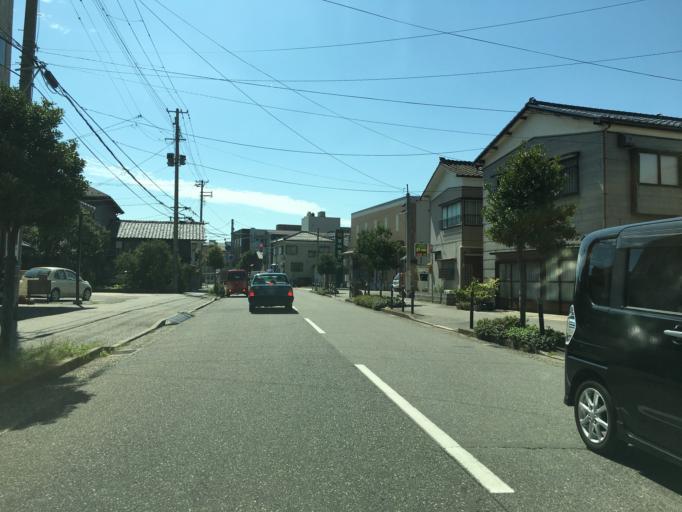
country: JP
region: Niigata
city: Niigata-shi
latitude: 37.9291
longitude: 139.0498
